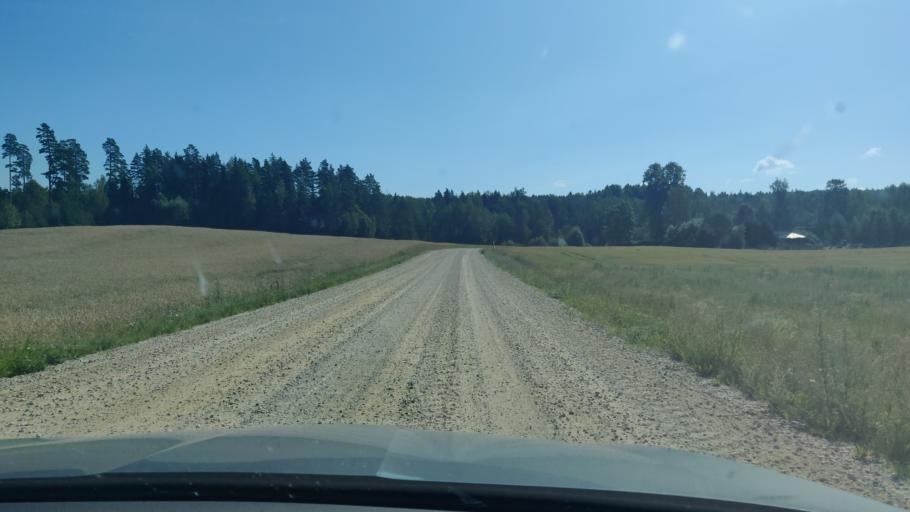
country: EE
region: Tartu
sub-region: Elva linn
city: Elva
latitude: 58.1336
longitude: 26.4054
